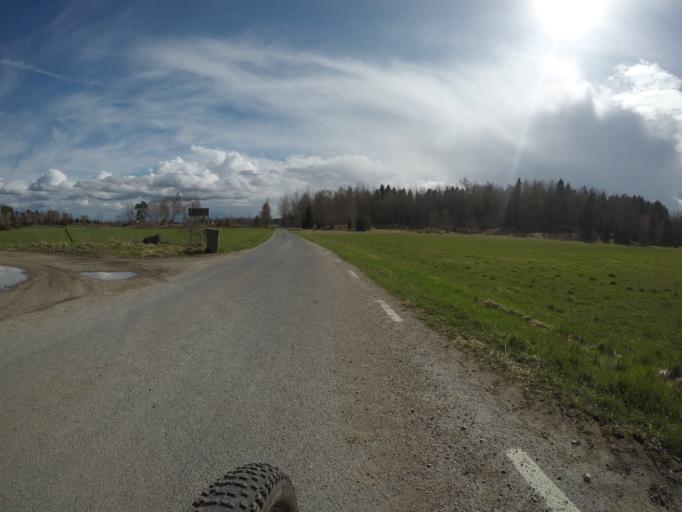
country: SE
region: Vaestmanland
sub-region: Kungsors Kommun
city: Kungsoer
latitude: 59.2965
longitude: 16.1413
